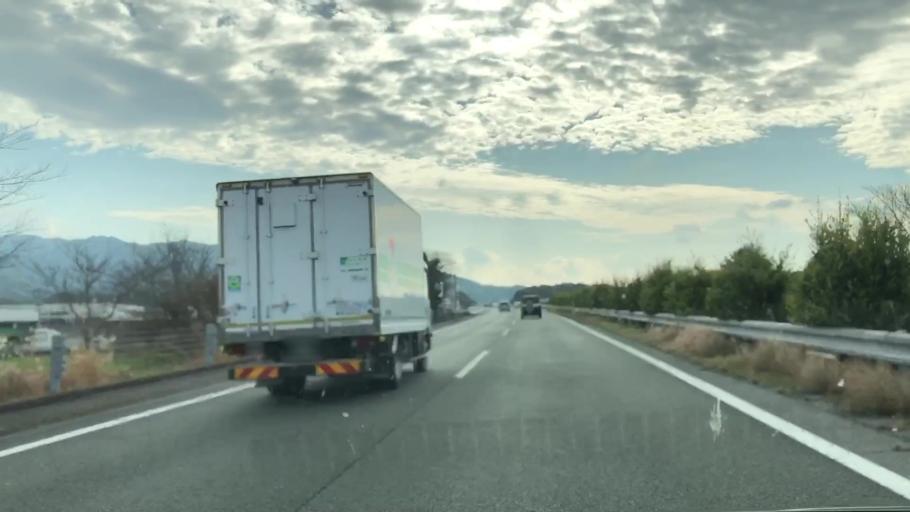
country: JP
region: Fukuoka
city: Setakamachi-takayanagi
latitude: 33.1881
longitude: 130.5195
